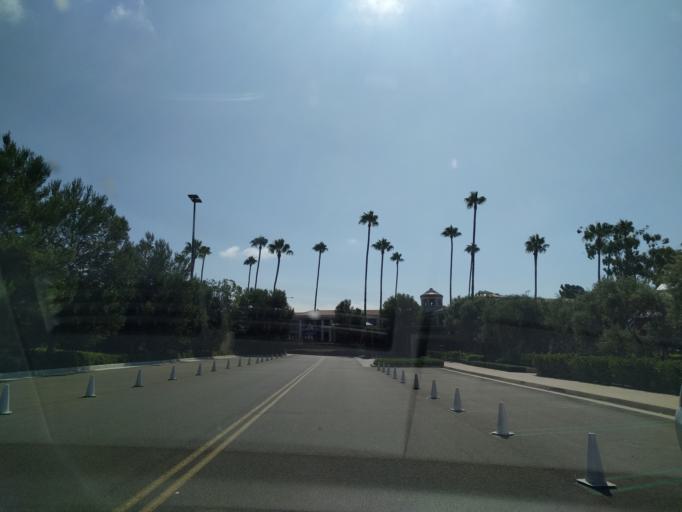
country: US
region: California
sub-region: Orange County
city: San Joaquin Hills
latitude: 33.6135
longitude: -117.8748
